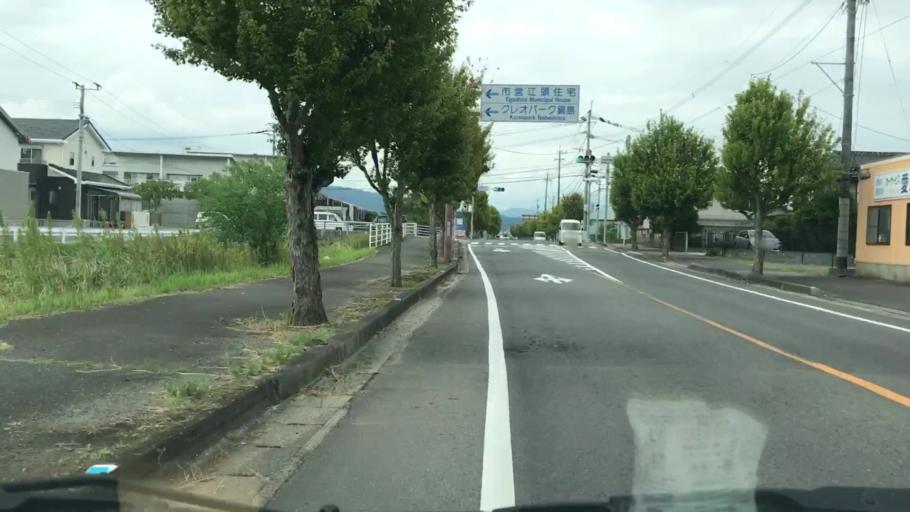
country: JP
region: Saga Prefecture
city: Saga-shi
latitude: 33.2644
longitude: 130.2626
